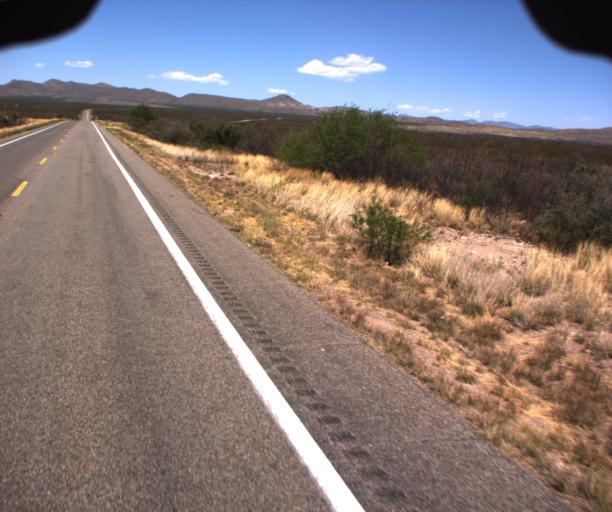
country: US
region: Arizona
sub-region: Cochise County
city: Tombstone
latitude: 31.6017
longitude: -110.0477
